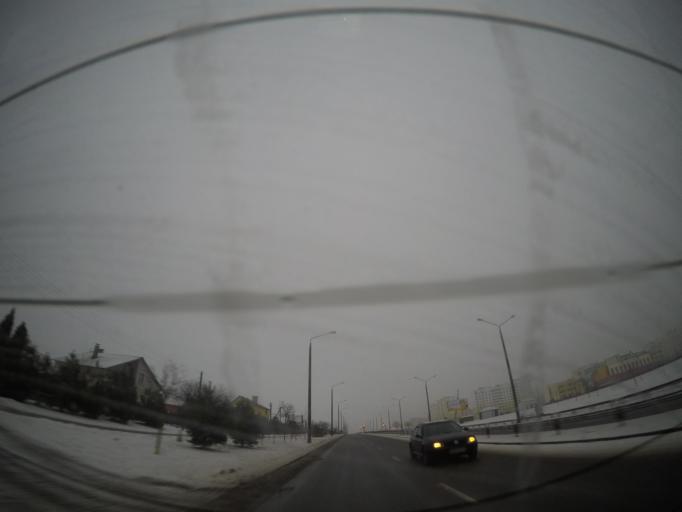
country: BY
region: Grodnenskaya
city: Hrodna
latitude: 53.6264
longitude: 23.8057
